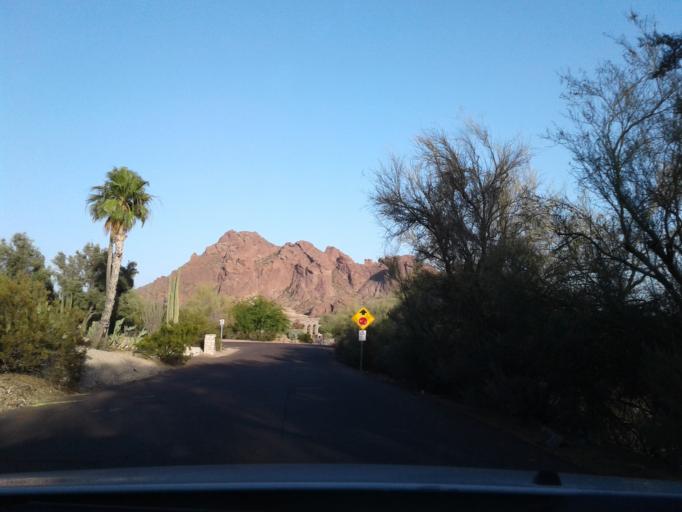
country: US
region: Arizona
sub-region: Maricopa County
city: Paradise Valley
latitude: 33.5261
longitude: -111.9873
